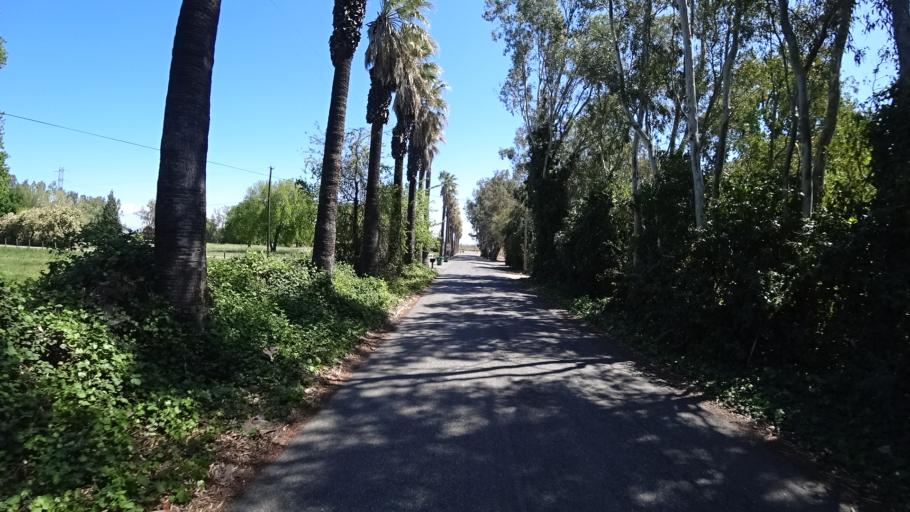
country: US
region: California
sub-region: Glenn County
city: Orland
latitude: 39.7963
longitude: -122.1840
